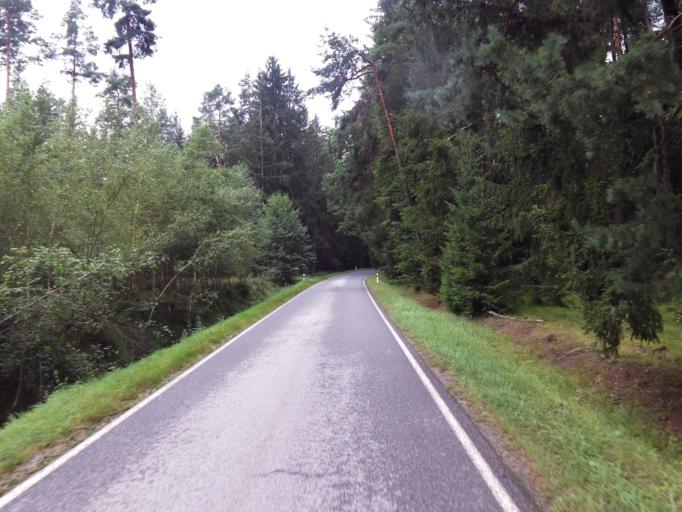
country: CZ
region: Jihocesky
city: Suchdol nad Luznici
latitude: 48.8621
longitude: 14.8422
